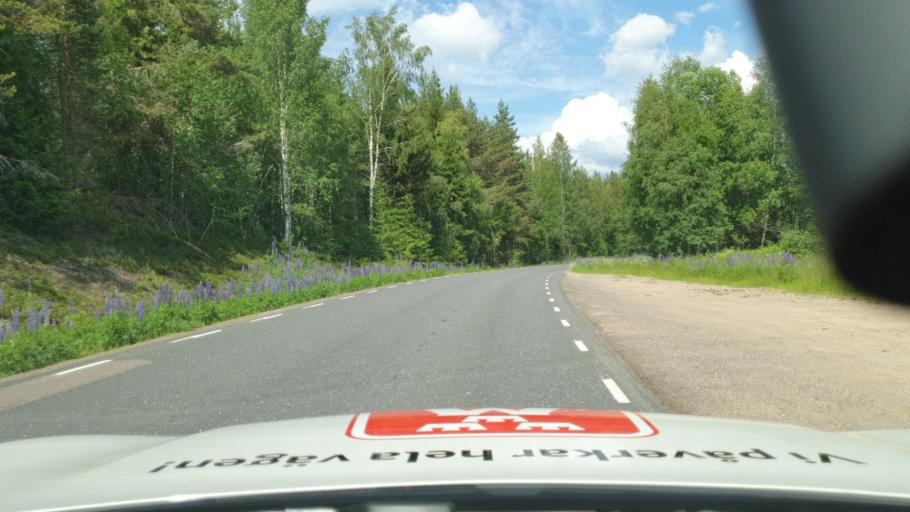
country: SE
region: Vaermland
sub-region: Torsby Kommun
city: Torsby
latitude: 60.6483
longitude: 12.6922
